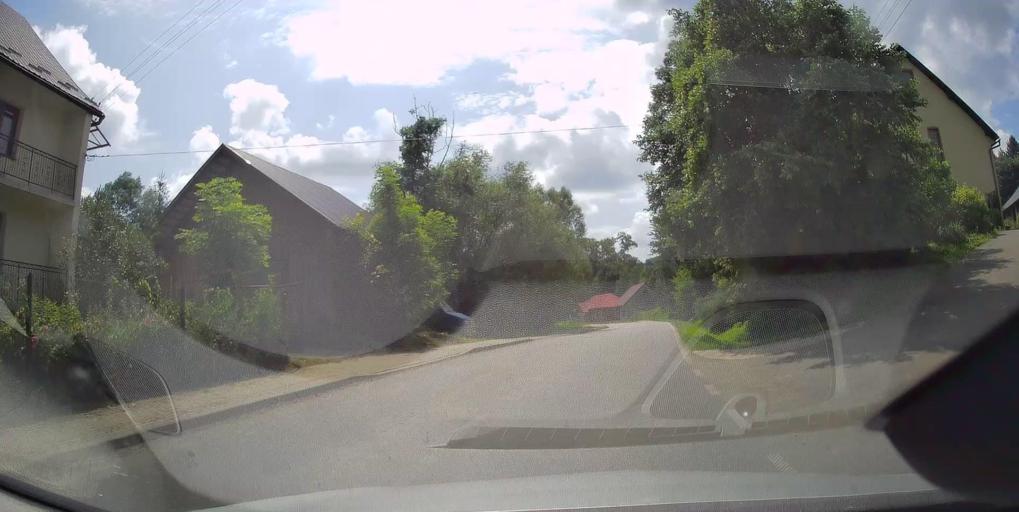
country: PL
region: Lesser Poland Voivodeship
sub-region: Powiat nowosadecki
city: Korzenna
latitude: 49.7362
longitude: 20.7725
